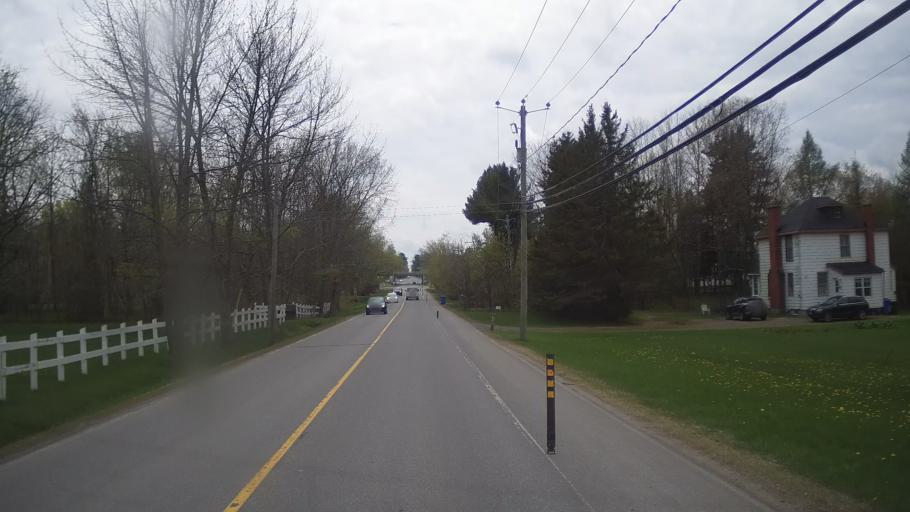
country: CA
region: Quebec
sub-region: Monteregie
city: Hudson
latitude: 45.4394
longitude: -74.1716
